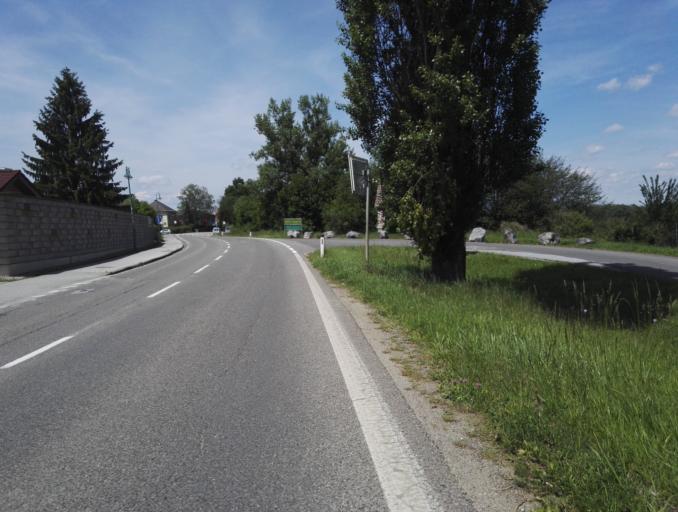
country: AT
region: Styria
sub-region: Politischer Bezirk Graz-Umgebung
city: Kalsdorf bei Graz
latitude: 46.9687
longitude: 15.4752
